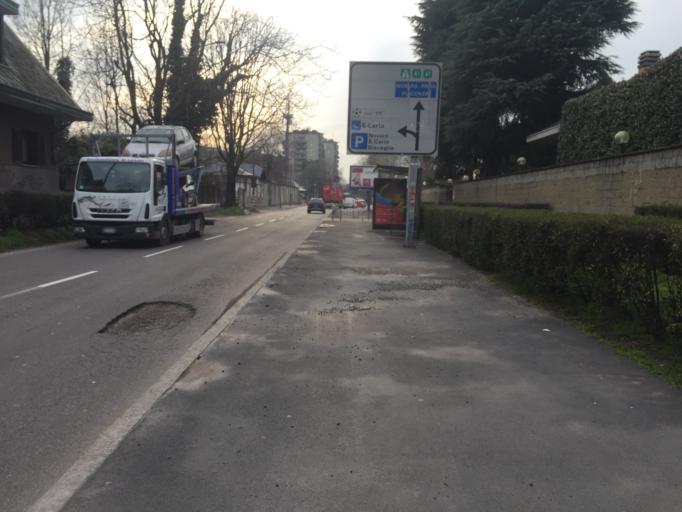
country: IT
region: Lombardy
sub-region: Citta metropolitana di Milano
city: Pero
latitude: 45.4853
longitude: 9.1203
